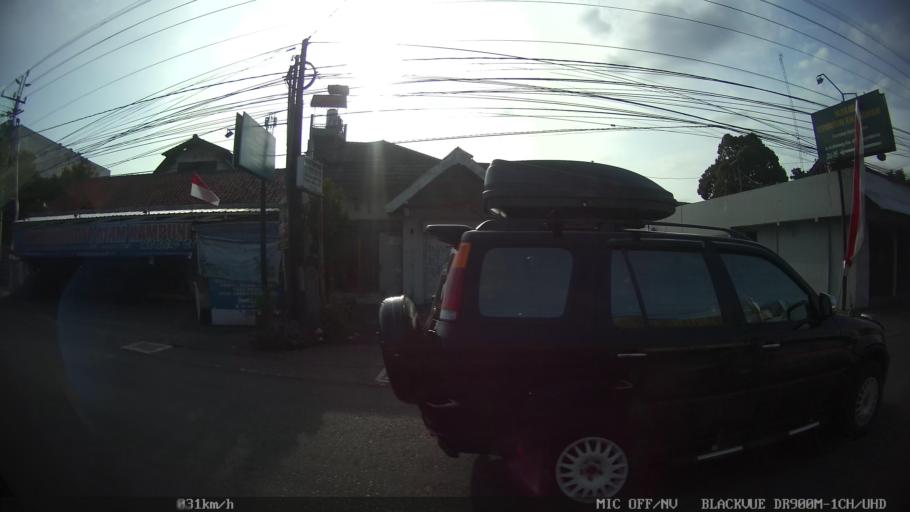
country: ID
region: Daerah Istimewa Yogyakarta
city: Melati
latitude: -7.7518
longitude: 110.3863
